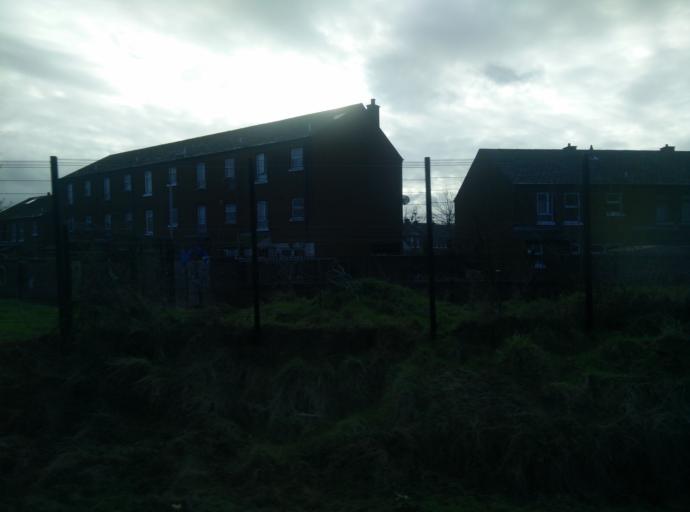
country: GB
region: Northern Ireland
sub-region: City of Belfast
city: Belfast
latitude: 54.5895
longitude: -5.9228
